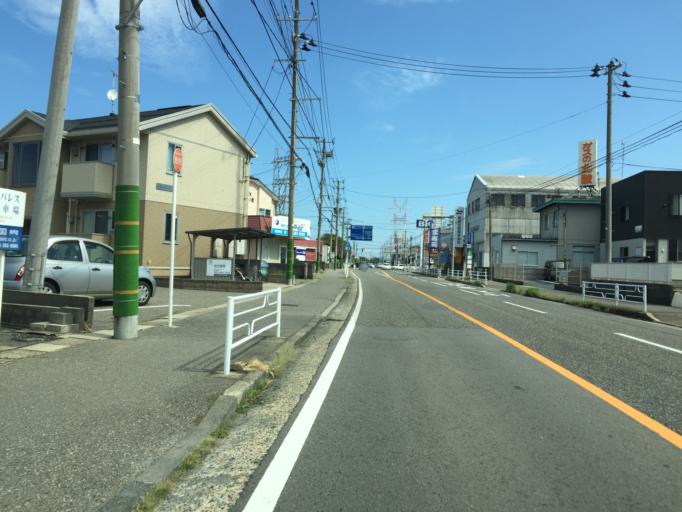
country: JP
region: Niigata
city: Niigata-shi
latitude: 37.9422
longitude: 139.0853
